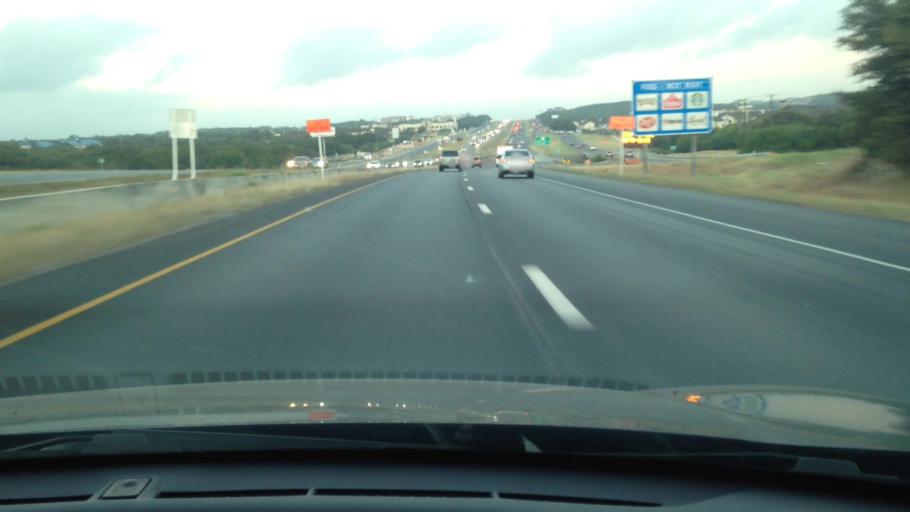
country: US
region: Texas
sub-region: Bexar County
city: Shavano Park
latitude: 29.6018
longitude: -98.5362
